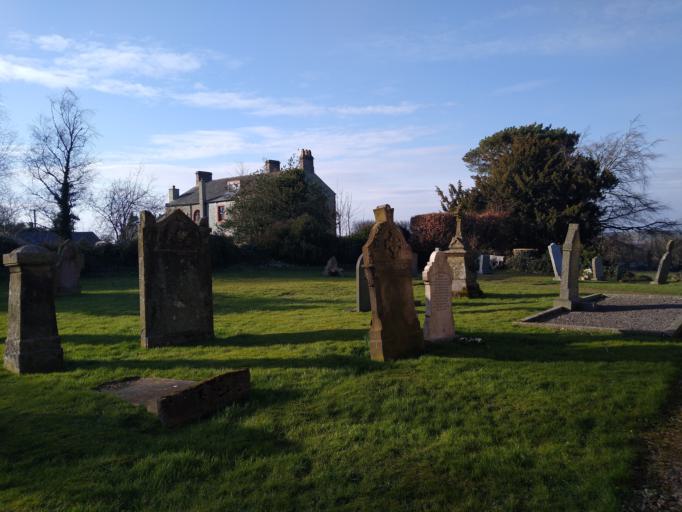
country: GB
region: England
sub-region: Cumbria
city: Aspatria
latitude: 54.7406
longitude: -3.3352
